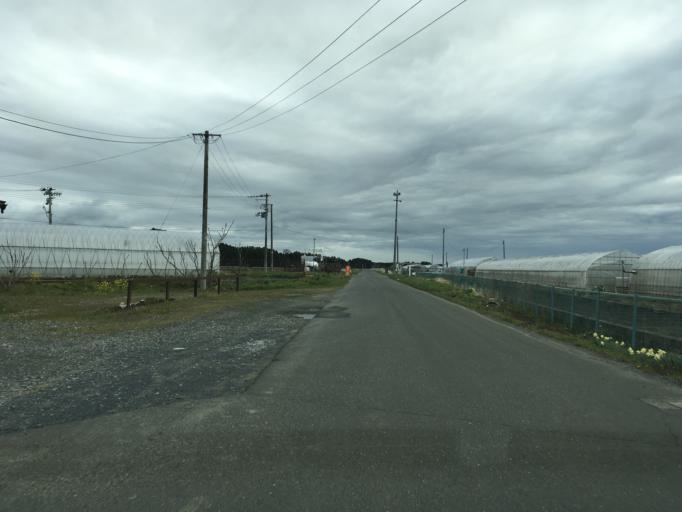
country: JP
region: Iwate
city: Ichinoseki
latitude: 38.7611
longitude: 141.2676
